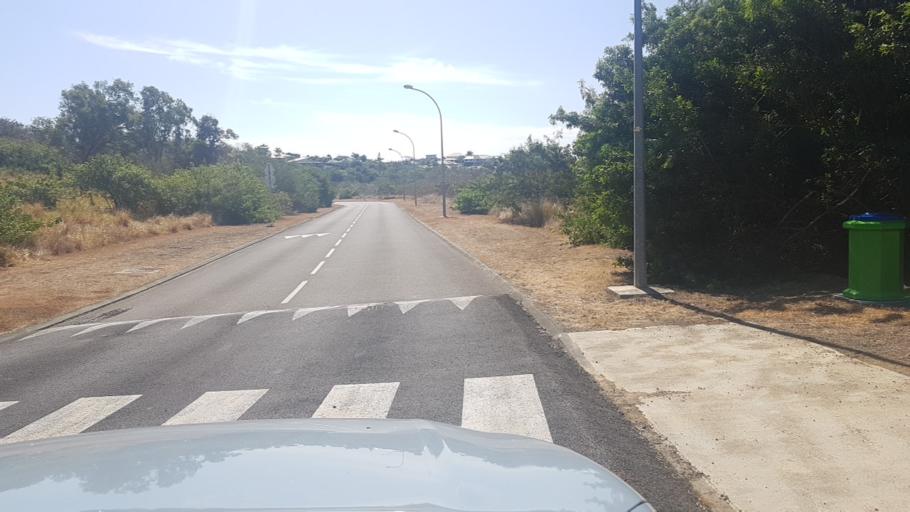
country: NC
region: South Province
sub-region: Dumbea
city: Dumbea
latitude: -22.1947
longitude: 166.4308
